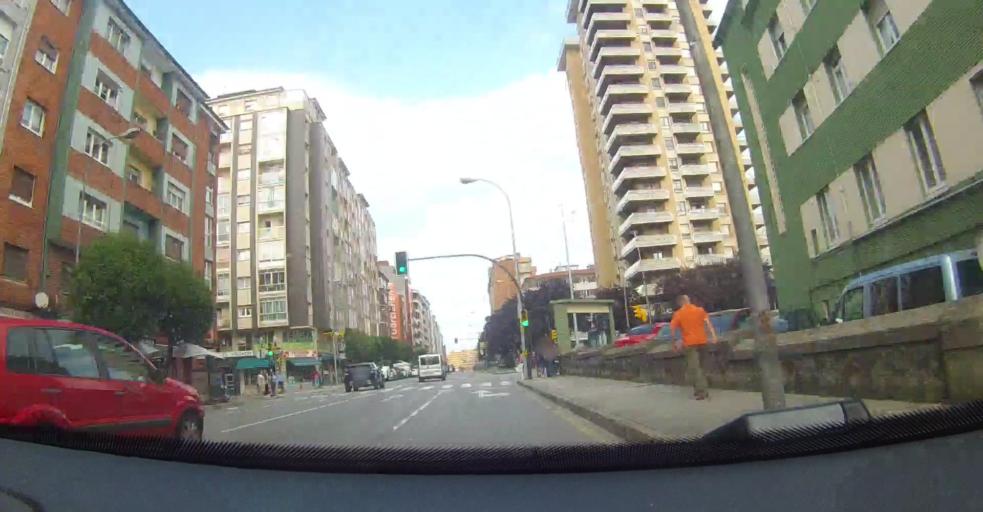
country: ES
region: Asturias
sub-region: Province of Asturias
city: Gijon
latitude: 43.5355
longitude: -5.6536
